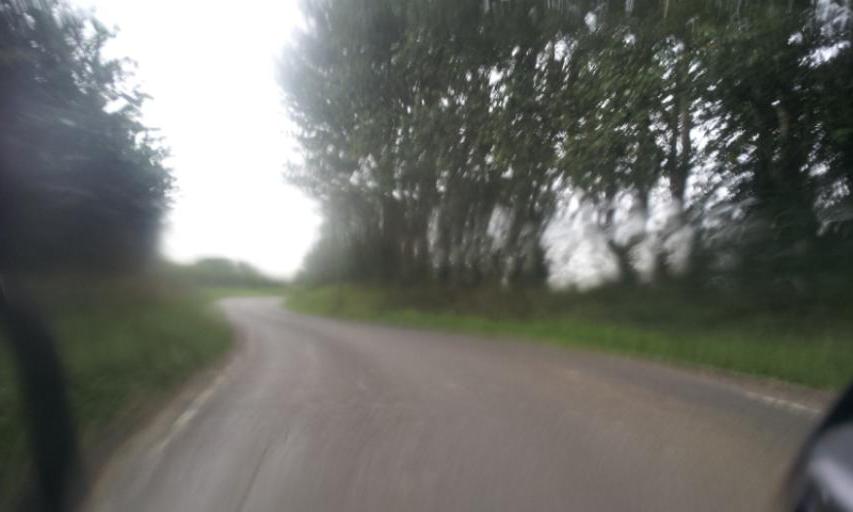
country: GB
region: England
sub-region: Kent
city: Hadlow
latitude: 51.2052
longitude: 0.3358
